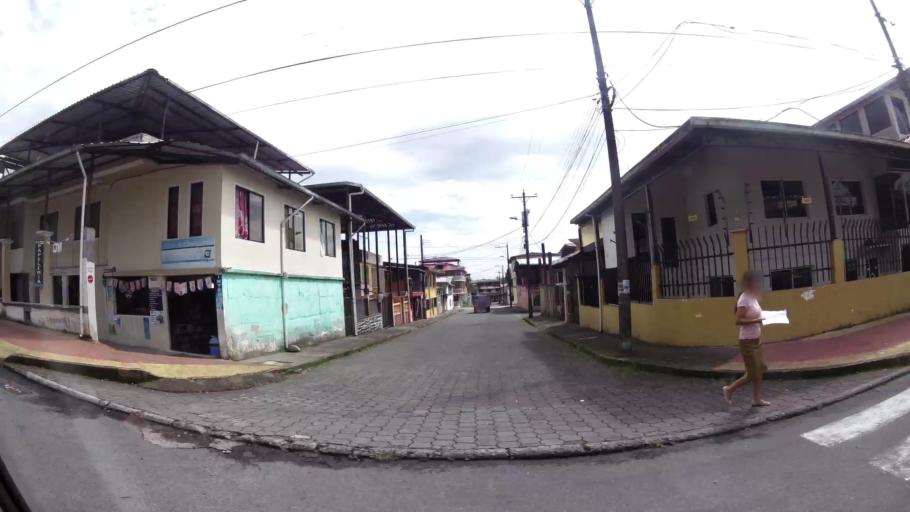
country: EC
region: Pastaza
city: Puyo
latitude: -1.4825
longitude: -78.0109
